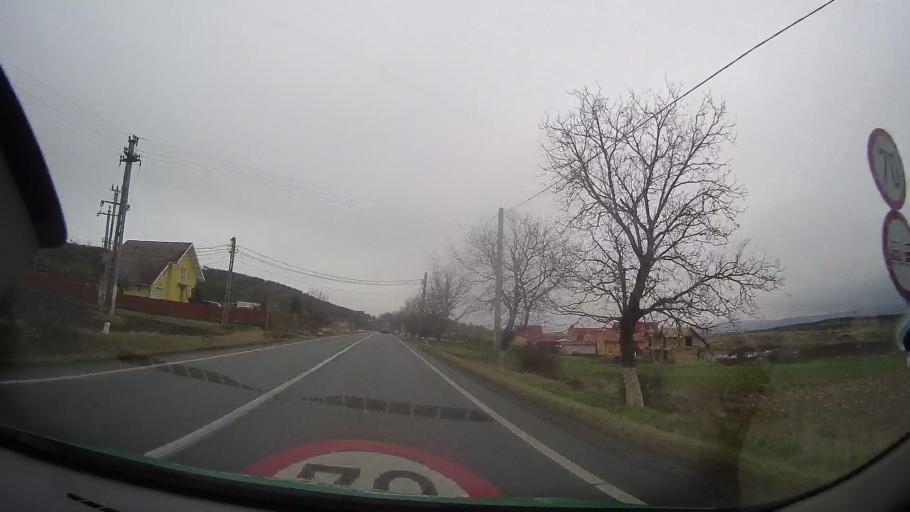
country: RO
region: Mures
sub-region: Comuna Breaza
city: Breaza
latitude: 46.7710
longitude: 24.6574
